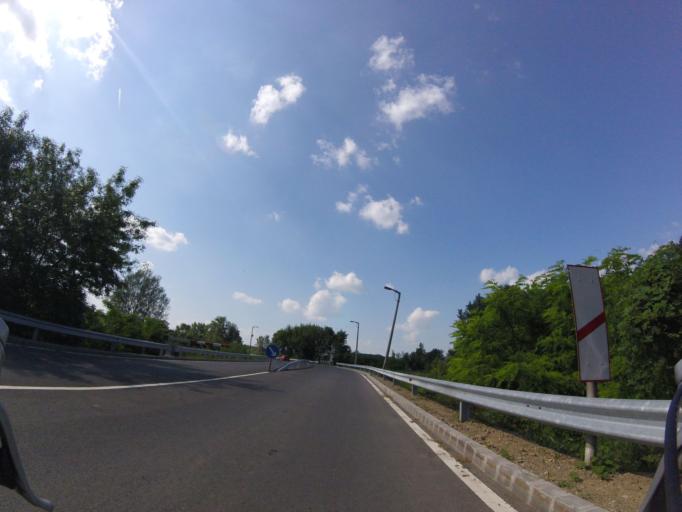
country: HU
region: Heves
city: Kiskore
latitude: 47.4765
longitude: 20.5187
